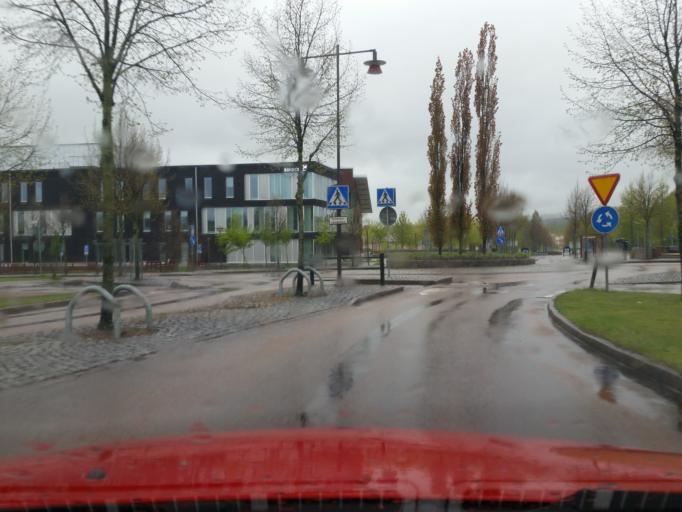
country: SE
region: Dalarna
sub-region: Borlange Kommun
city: Borlaenge
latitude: 60.4865
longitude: 15.4120
